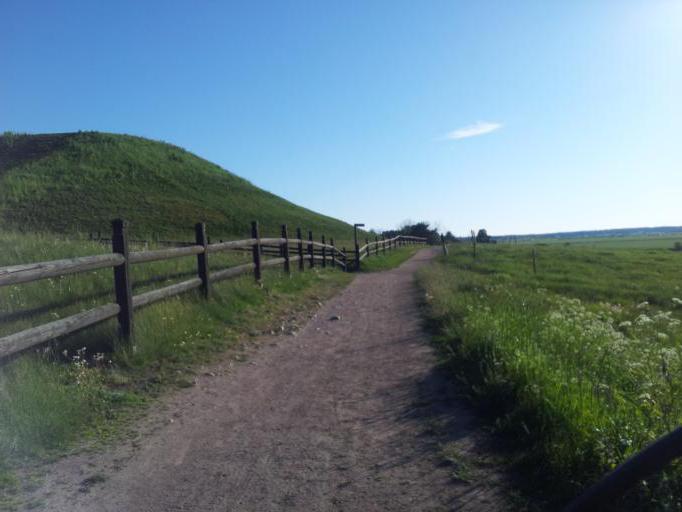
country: SE
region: Uppsala
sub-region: Uppsala Kommun
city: Gamla Uppsala
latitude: 59.8983
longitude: 17.6294
